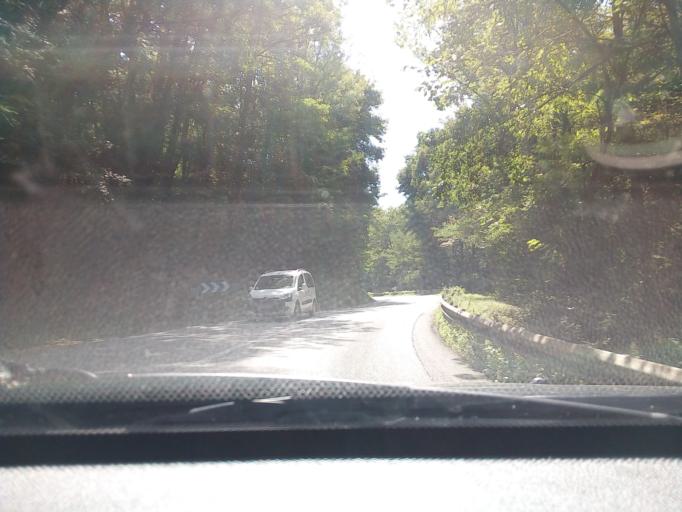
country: FR
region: Rhone-Alpes
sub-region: Departement de l'Isere
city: Poisat
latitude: 45.1435
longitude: 5.7698
